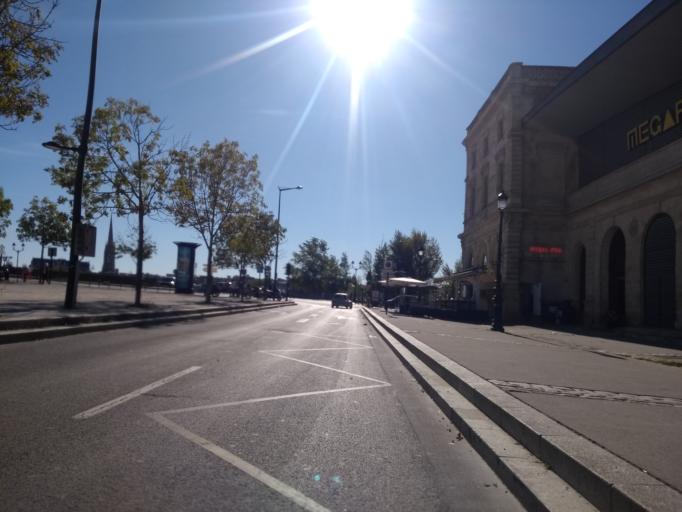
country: FR
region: Aquitaine
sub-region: Departement de la Gironde
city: Bordeaux
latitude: 44.8416
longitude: -0.5614
